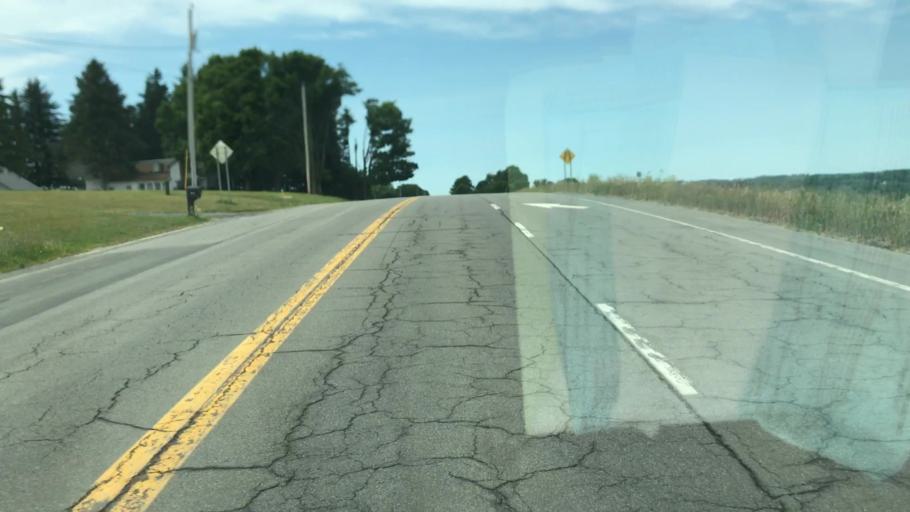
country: US
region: New York
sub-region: Onondaga County
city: Marcellus
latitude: 42.9357
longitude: -76.3649
